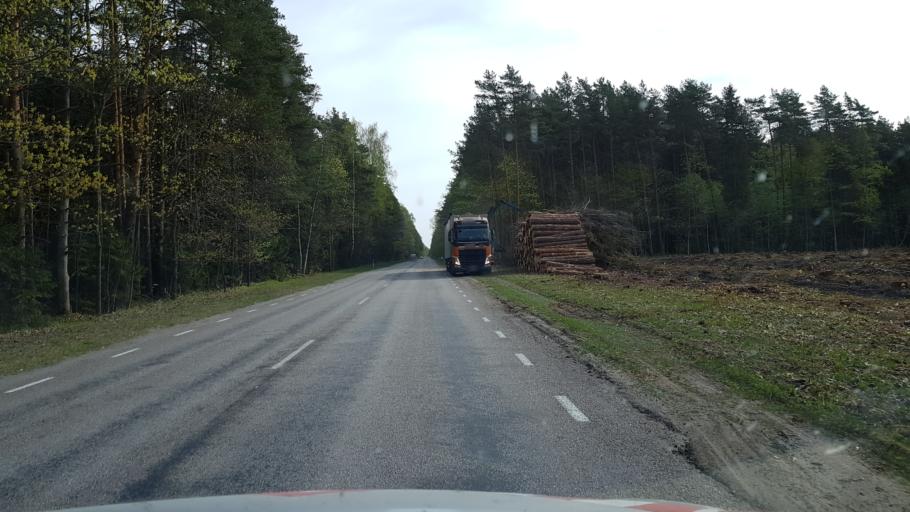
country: EE
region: Paernumaa
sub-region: Audru vald
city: Audru
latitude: 58.4083
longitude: 24.3319
